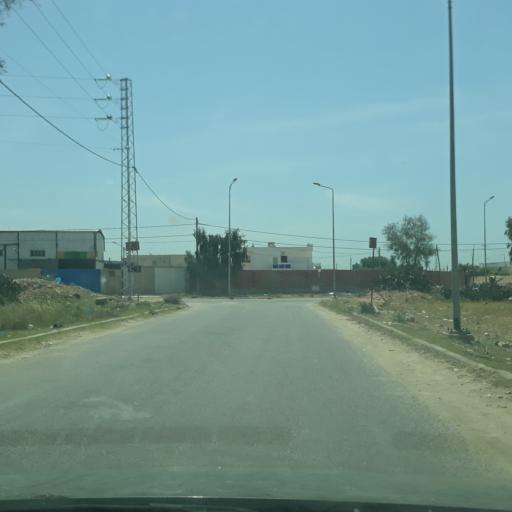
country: TN
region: Safaqis
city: Al Qarmadah
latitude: 34.8243
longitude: 10.7863
